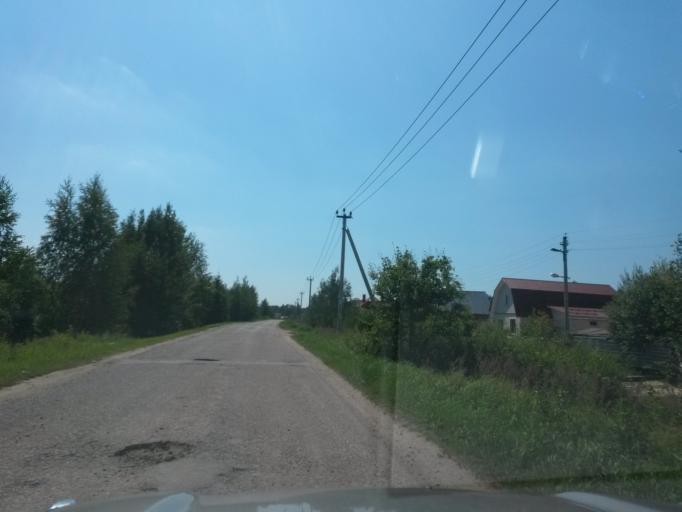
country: RU
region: Moskovskaya
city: Stolbovaya
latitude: 55.2649
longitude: 37.4880
